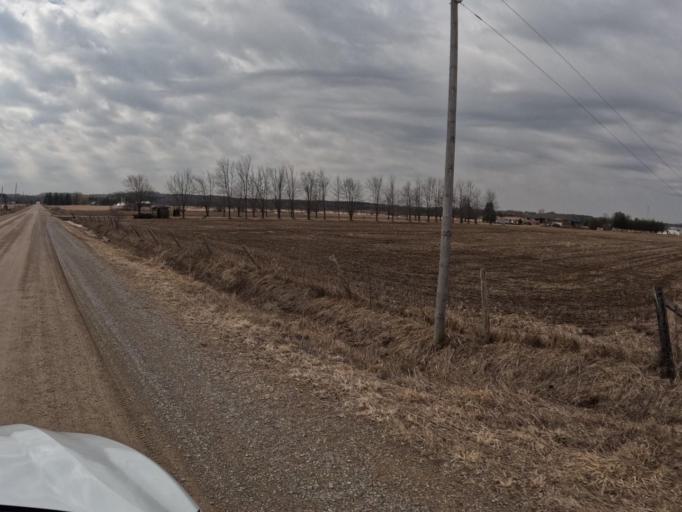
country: CA
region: Ontario
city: Orangeville
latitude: 43.9073
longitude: -80.2148
